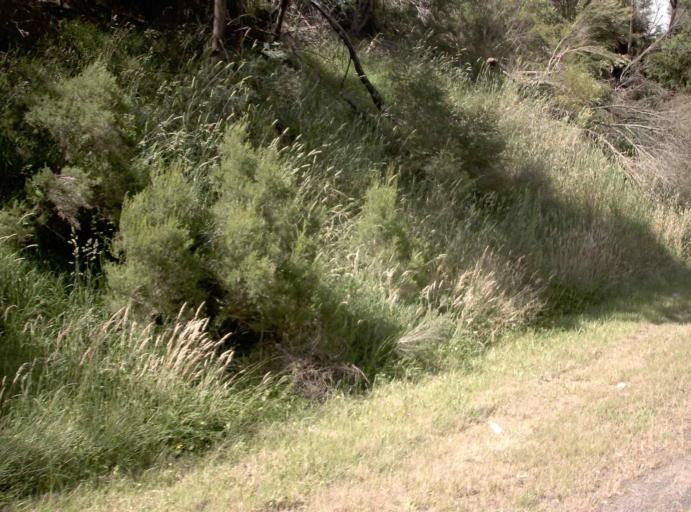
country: AU
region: Victoria
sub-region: Latrobe
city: Morwell
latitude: -38.1574
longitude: 146.4249
